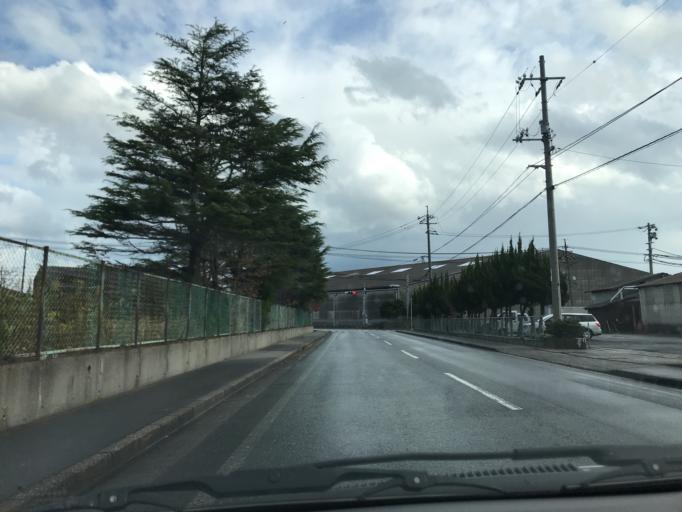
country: JP
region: Shimane
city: Sakaiminato
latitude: 35.5418
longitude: 133.2486
